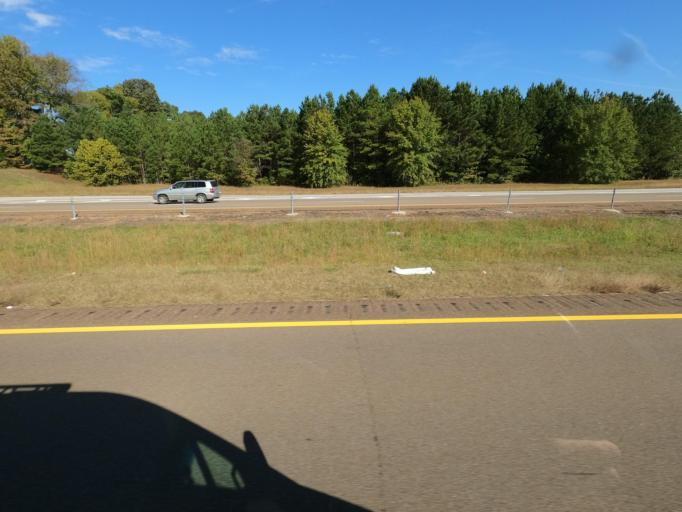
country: US
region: Tennessee
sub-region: Shelby County
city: Lakeland
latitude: 35.3099
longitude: -89.7574
